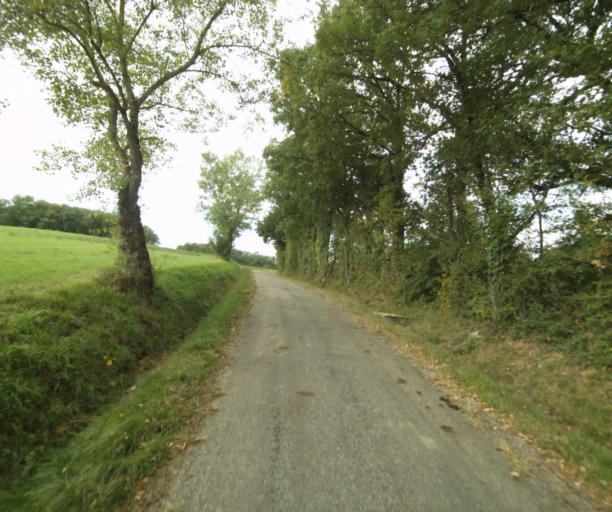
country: FR
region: Midi-Pyrenees
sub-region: Departement du Gers
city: Gondrin
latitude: 43.8649
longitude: 0.2597
